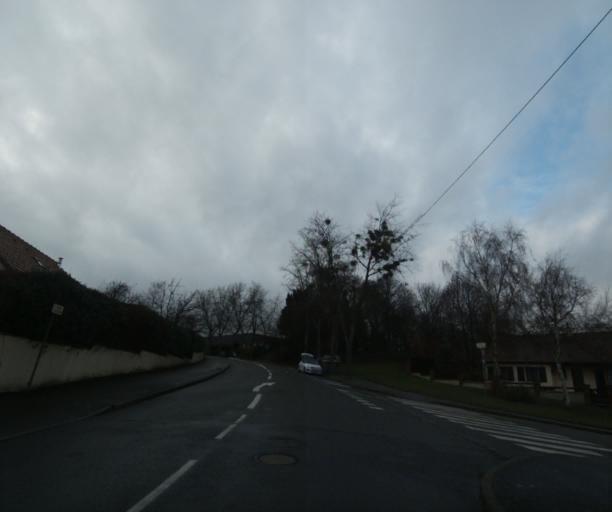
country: FR
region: Pays de la Loire
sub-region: Departement de la Sarthe
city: Coulaines
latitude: 48.0278
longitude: 0.1851
